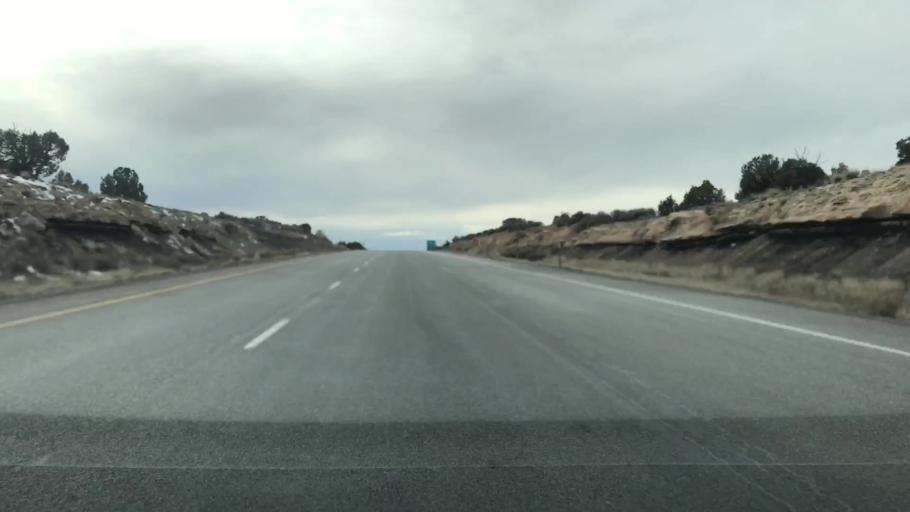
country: US
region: Colorado
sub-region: Mesa County
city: Loma
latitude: 39.1817
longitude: -109.1211
